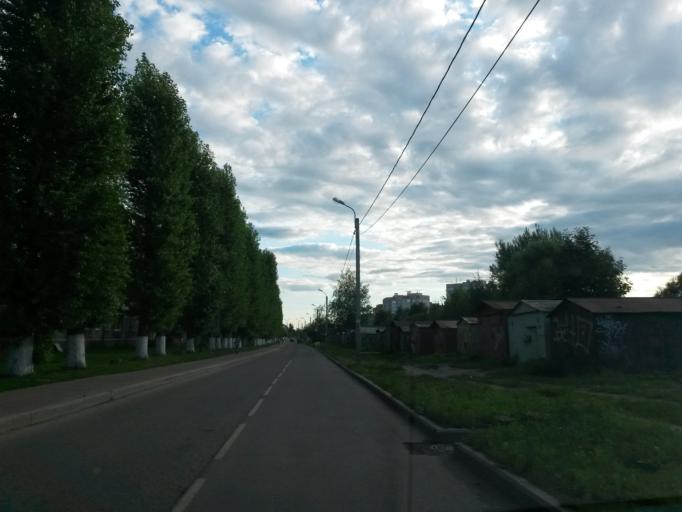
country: RU
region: Jaroslavl
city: Yaroslavl
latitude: 57.6864
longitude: 39.7730
